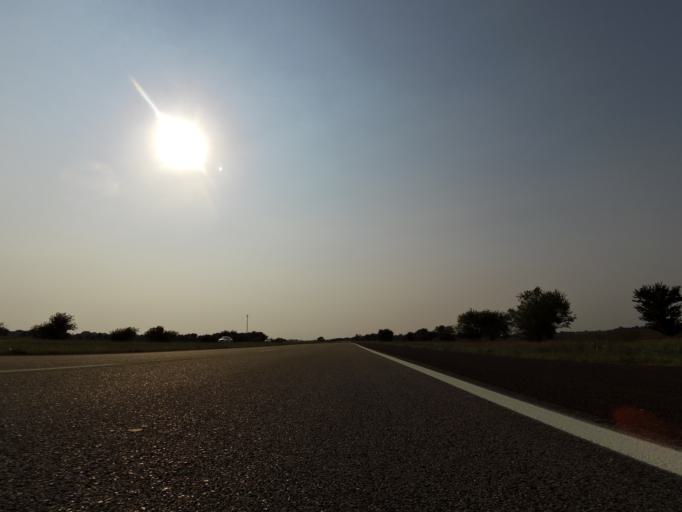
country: US
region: Kansas
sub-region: Reno County
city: Haven
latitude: 37.8926
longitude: -97.7600
